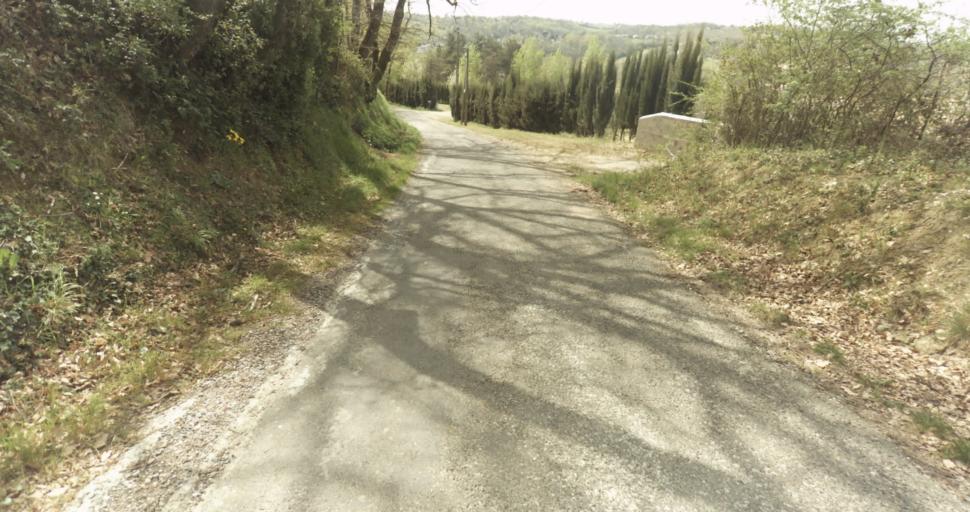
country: FR
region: Midi-Pyrenees
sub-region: Departement du Tarn-et-Garonne
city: Moissac
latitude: 44.1230
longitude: 1.1100
